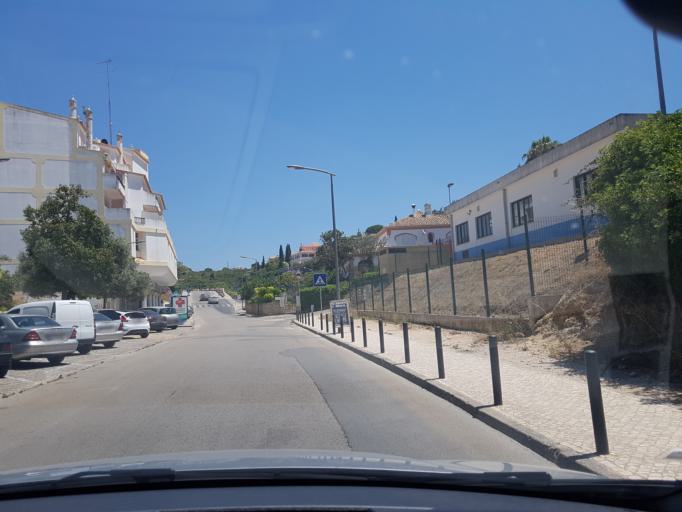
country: PT
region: Faro
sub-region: Lagoa
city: Carvoeiro
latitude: 37.1006
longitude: -8.4677
